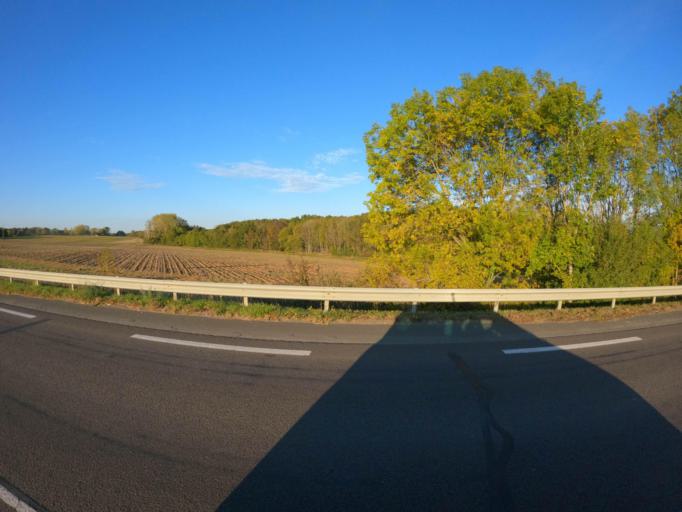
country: FR
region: Pays de la Loire
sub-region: Departement de la Vendee
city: Sainte-Hermine
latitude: 46.5687
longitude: -1.0499
